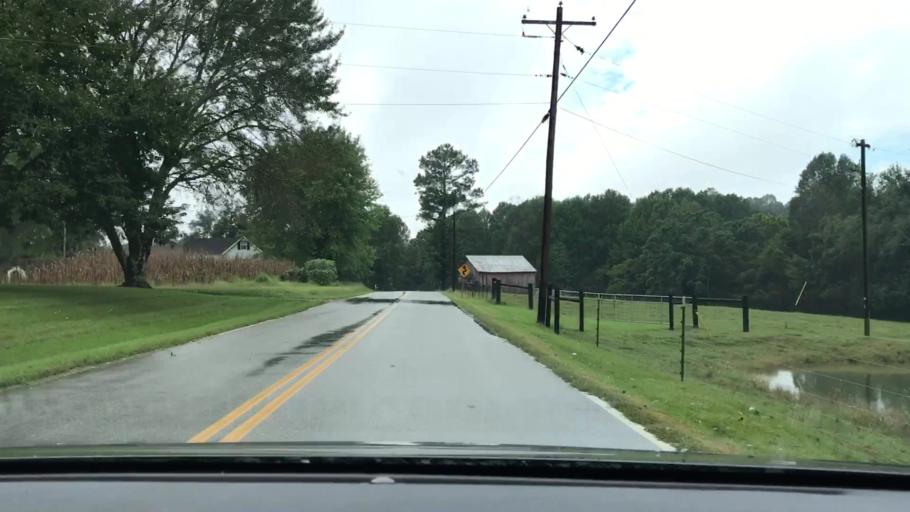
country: US
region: Tennessee
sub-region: Macon County
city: Red Boiling Springs
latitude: 36.4352
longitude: -85.8915
